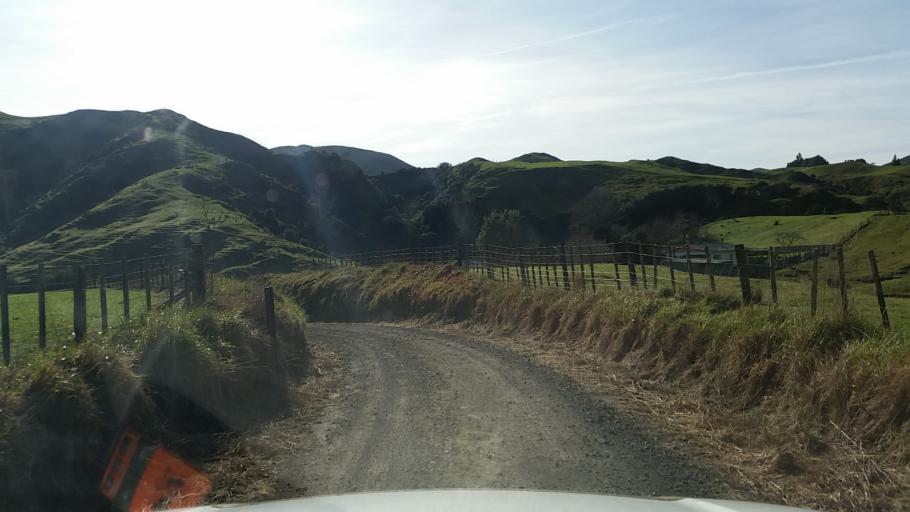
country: NZ
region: Taranaki
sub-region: South Taranaki District
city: Eltham
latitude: -39.3111
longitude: 174.5494
